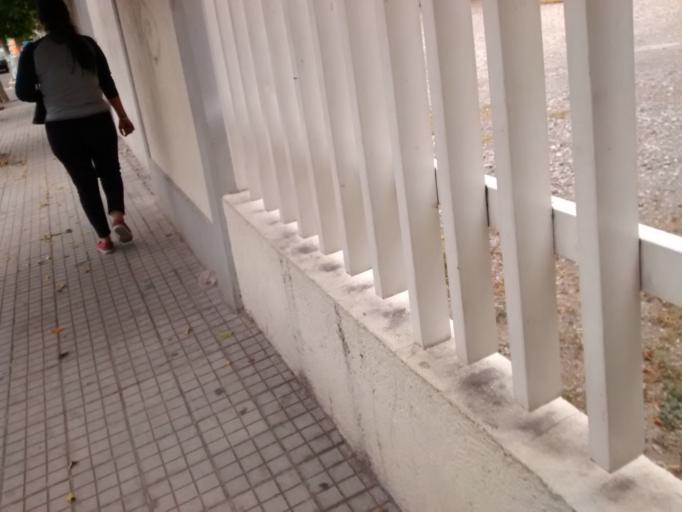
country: MX
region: Puebla
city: Tehuacan
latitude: 18.4564
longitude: -97.3909
